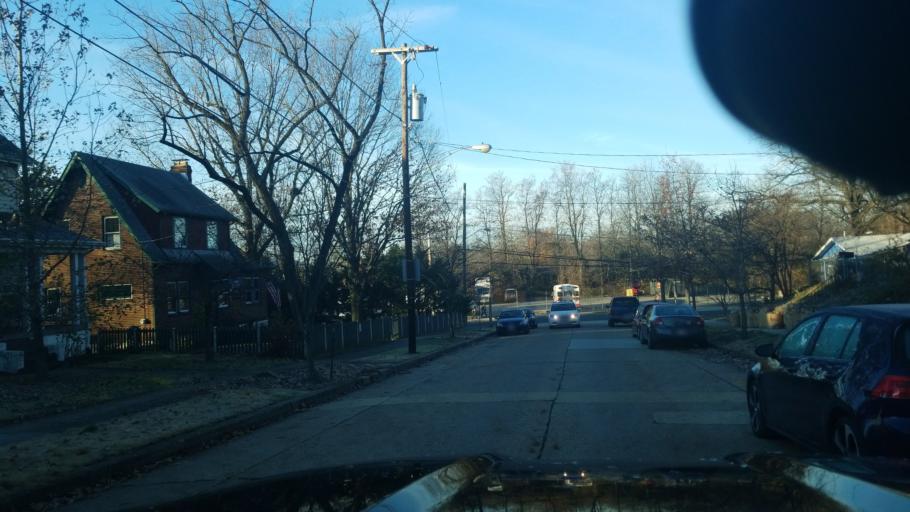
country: US
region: Maryland
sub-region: Montgomery County
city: Takoma Park
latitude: 38.9710
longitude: -77.0138
